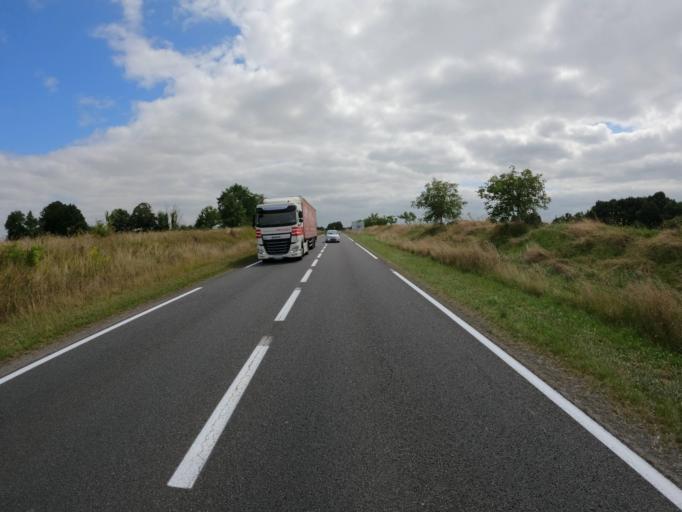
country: FR
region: Poitou-Charentes
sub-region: Departement de la Vienne
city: Charroux
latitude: 46.1516
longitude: 0.4030
